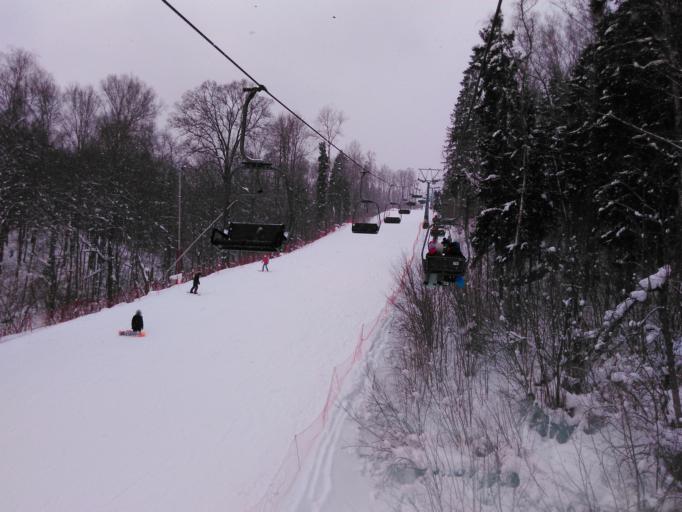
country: RU
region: Moskovskaya
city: Yakhroma
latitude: 56.2563
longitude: 37.4349
